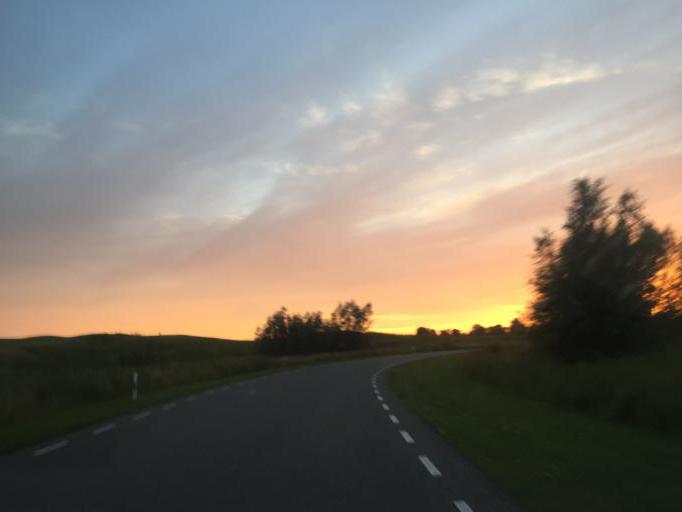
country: NL
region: Friesland
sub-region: Gemeente Dongeradeel
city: Anjum
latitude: 53.3753
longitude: 6.1547
